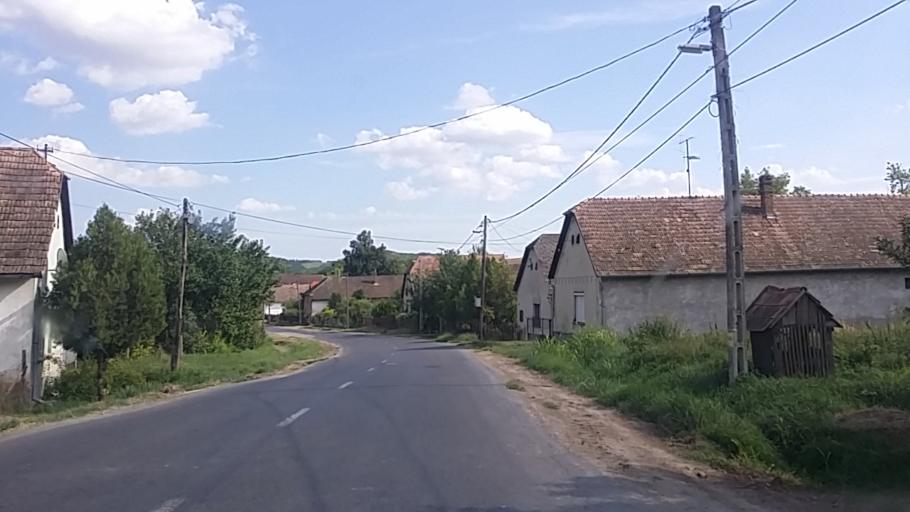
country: HU
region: Tolna
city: Gyonk
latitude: 46.5069
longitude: 18.5588
